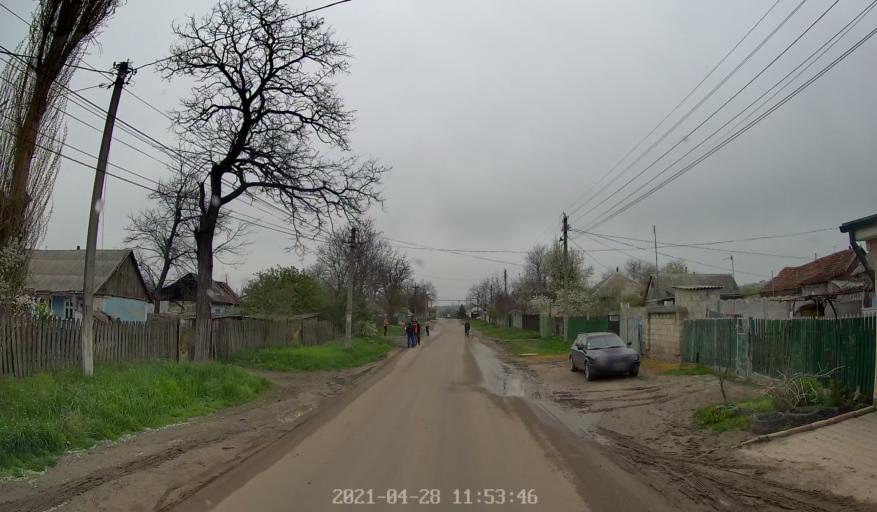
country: MD
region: Chisinau
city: Singera
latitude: 46.9567
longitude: 28.9409
